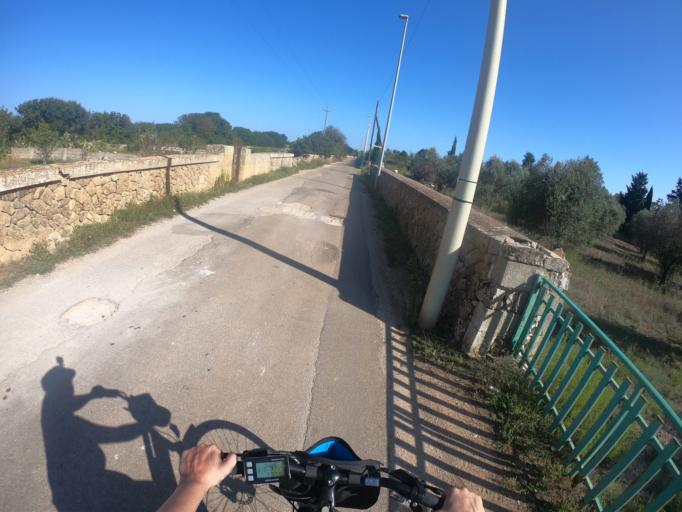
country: IT
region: Apulia
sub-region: Provincia di Lecce
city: Alessano
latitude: 39.8874
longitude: 18.3249
